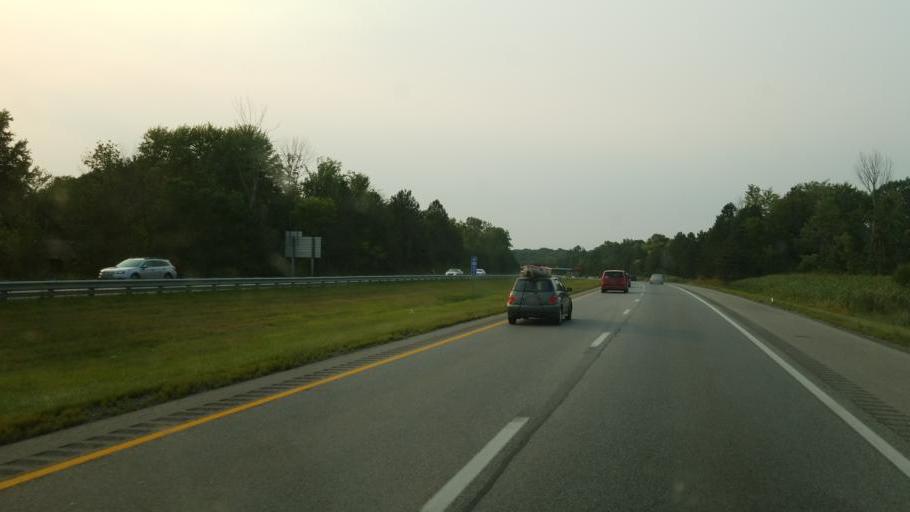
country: US
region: Ohio
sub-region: Cuyahoga County
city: Orange
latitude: 41.4194
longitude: -81.4768
